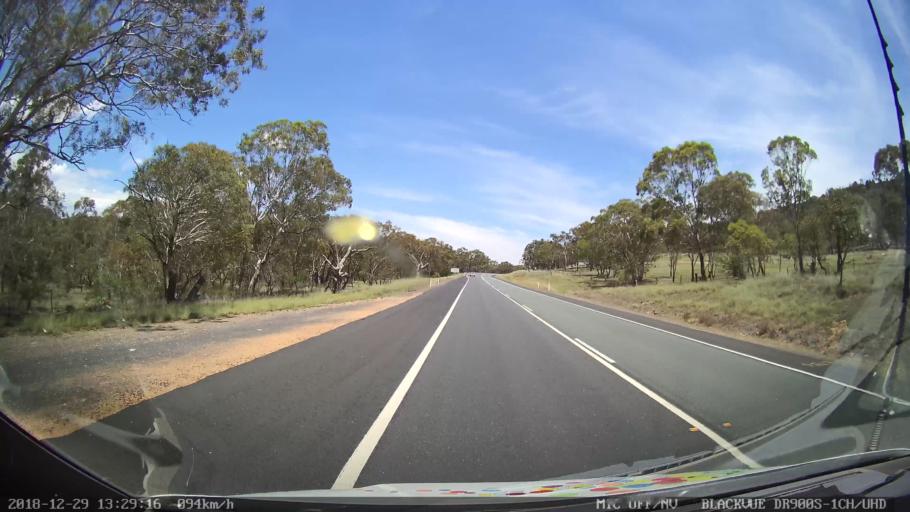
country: AU
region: New South Wales
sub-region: Cooma-Monaro
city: Cooma
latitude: -35.8877
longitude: 149.1616
